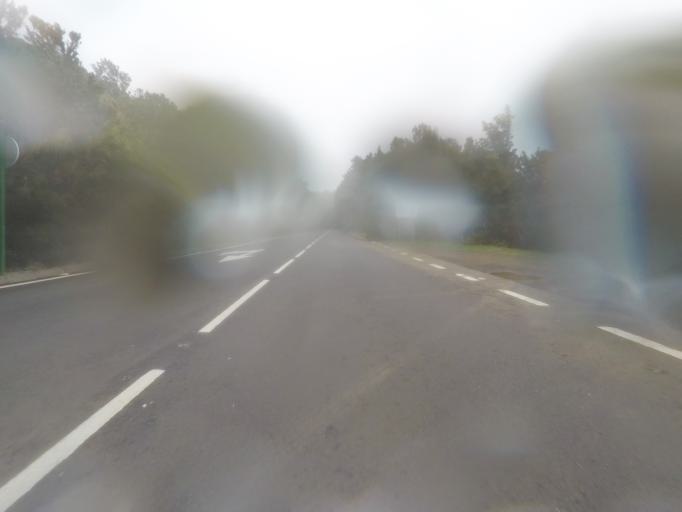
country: ES
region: Canary Islands
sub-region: Provincia de Santa Cruz de Tenerife
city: Vallehermosa
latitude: 28.1359
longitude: -17.2812
